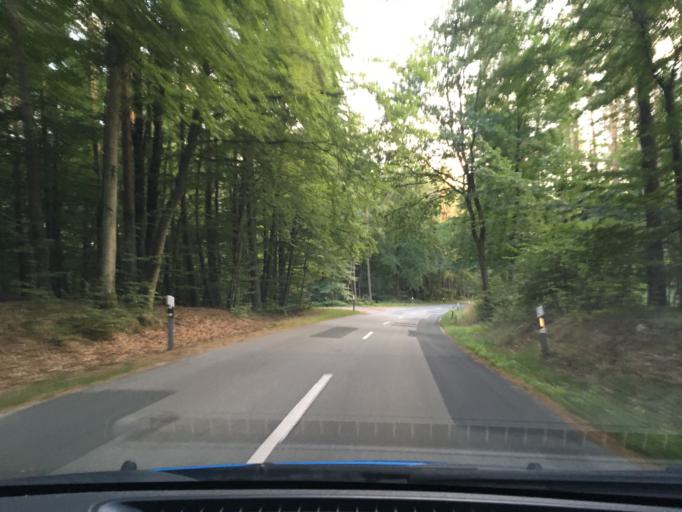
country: DE
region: Lower Saxony
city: Tosterglope
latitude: 53.2551
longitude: 10.8020
